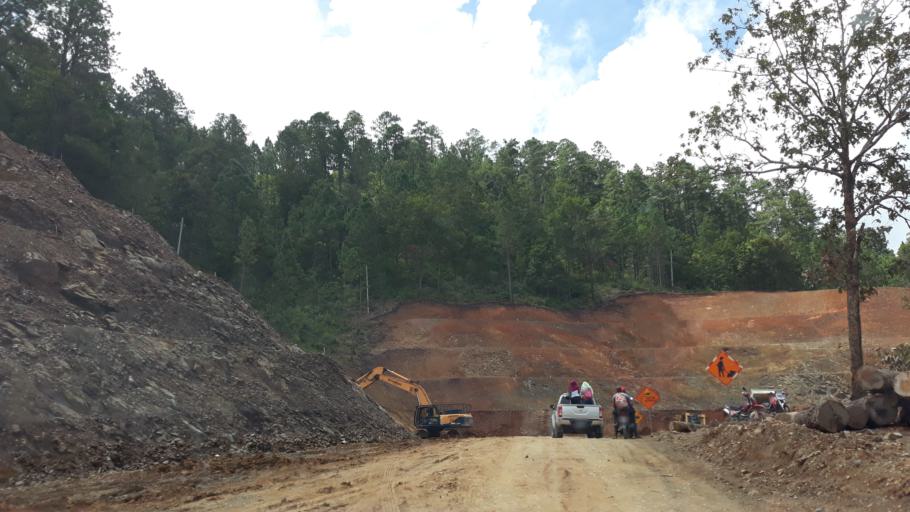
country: HN
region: El Paraiso
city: Santa Cruz
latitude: 13.7597
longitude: -86.6496
